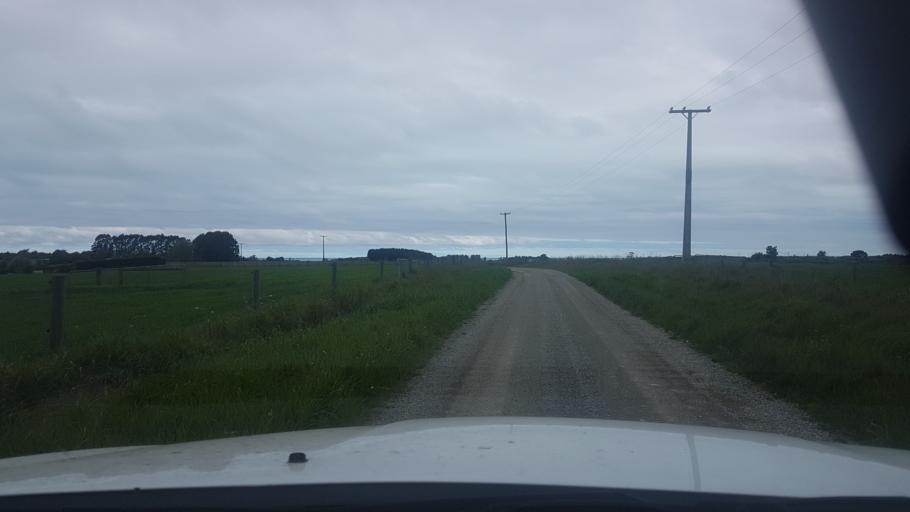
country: NZ
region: Canterbury
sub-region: Timaru District
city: Timaru
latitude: -44.4451
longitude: 171.2064
